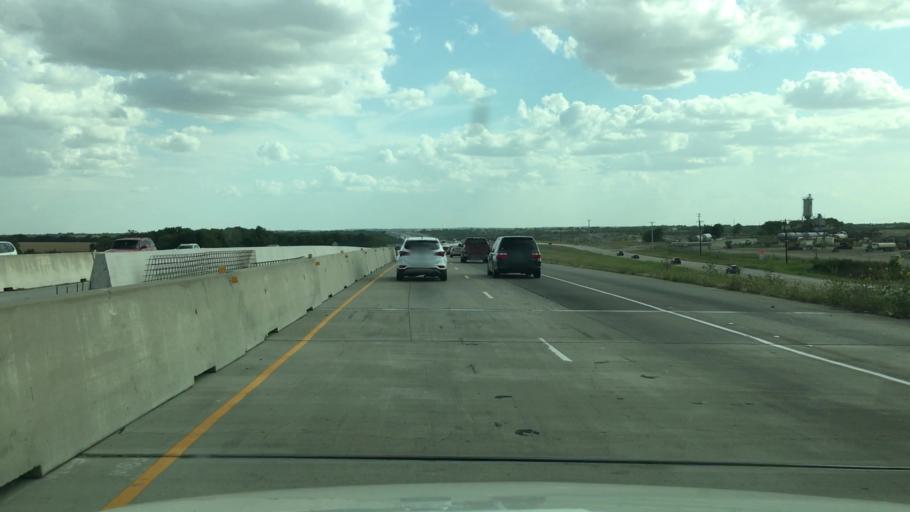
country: US
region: Texas
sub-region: McLennan County
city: Bruceville-Eddy
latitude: 31.2810
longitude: -97.2592
